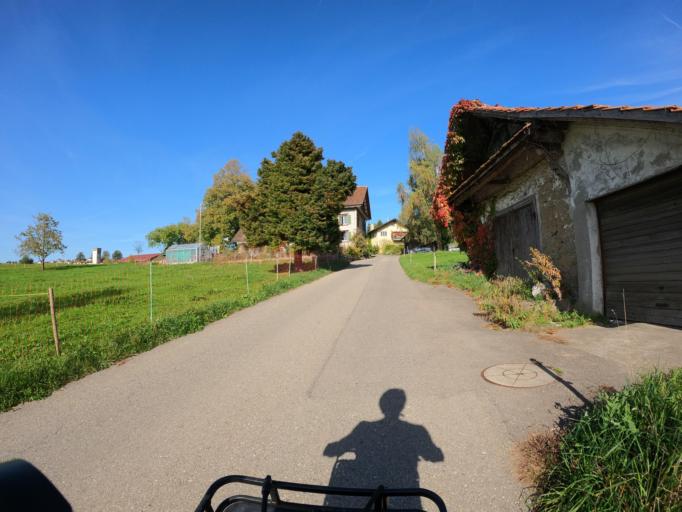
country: CH
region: Zug
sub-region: Zug
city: Baar
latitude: 47.2161
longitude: 8.5562
